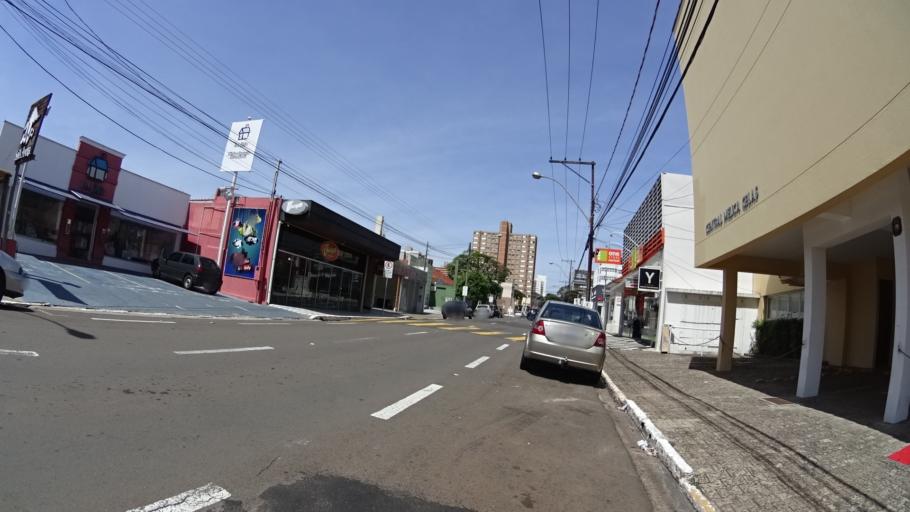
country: BR
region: Sao Paulo
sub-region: Marilia
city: Marilia
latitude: -22.2197
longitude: -49.9451
